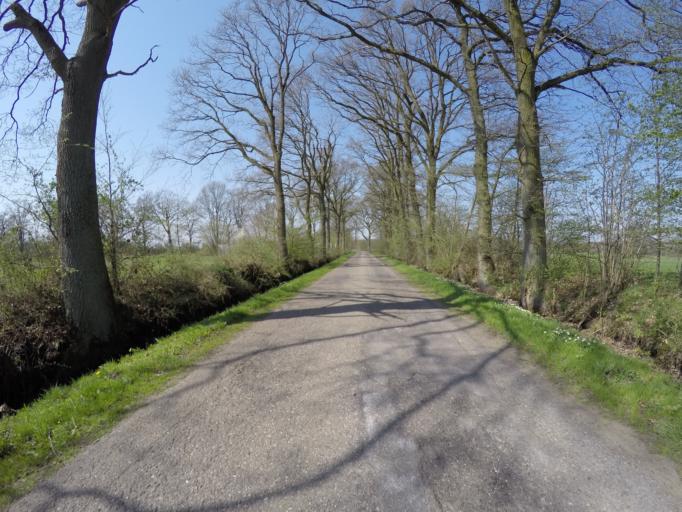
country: DE
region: Schleswig-Holstein
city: Ellerau
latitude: 53.7470
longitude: 9.8991
